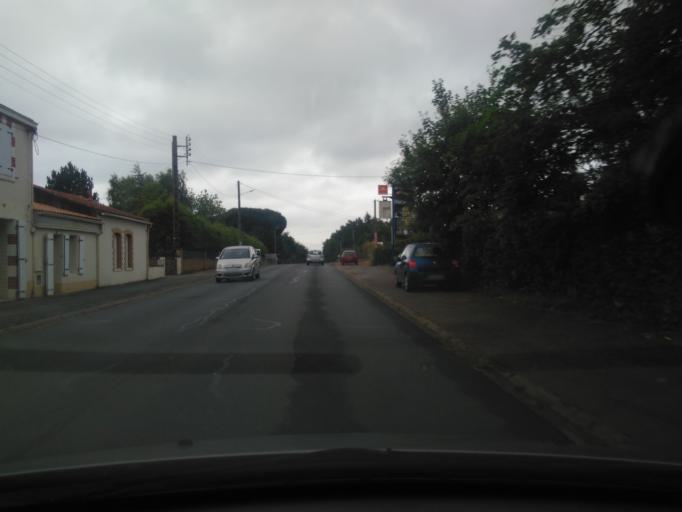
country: FR
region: Pays de la Loire
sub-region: Departement de la Vendee
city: Saint-Florent-des-Bois
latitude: 46.5897
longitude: -1.3101
